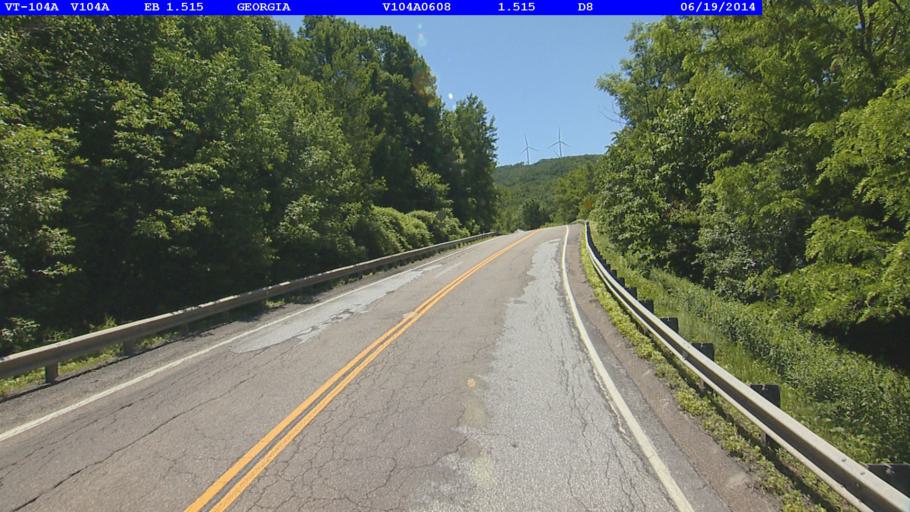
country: US
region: Vermont
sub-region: Chittenden County
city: Milton
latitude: 44.6817
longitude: -73.0853
